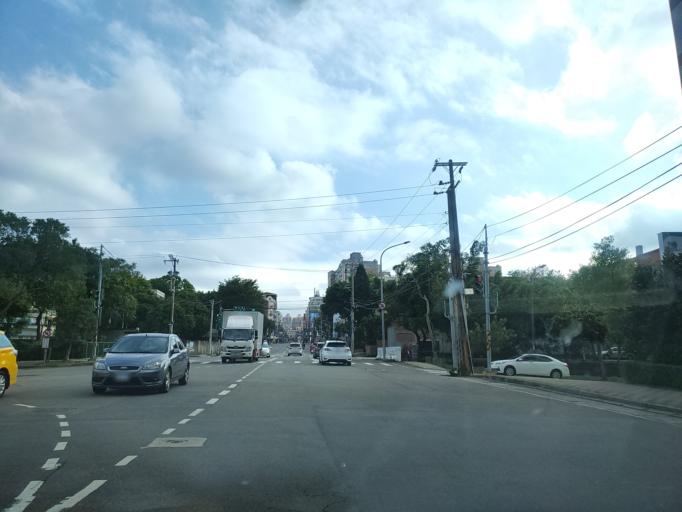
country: TW
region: Taiwan
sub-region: Hsinchu
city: Hsinchu
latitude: 24.8010
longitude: 120.9970
